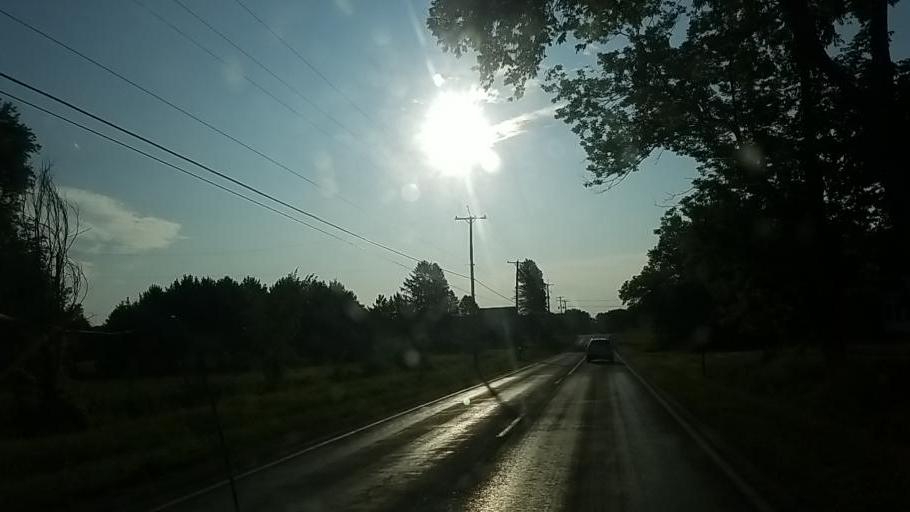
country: US
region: Michigan
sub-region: Montcalm County
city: Stanton
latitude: 43.2500
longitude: -85.1037
